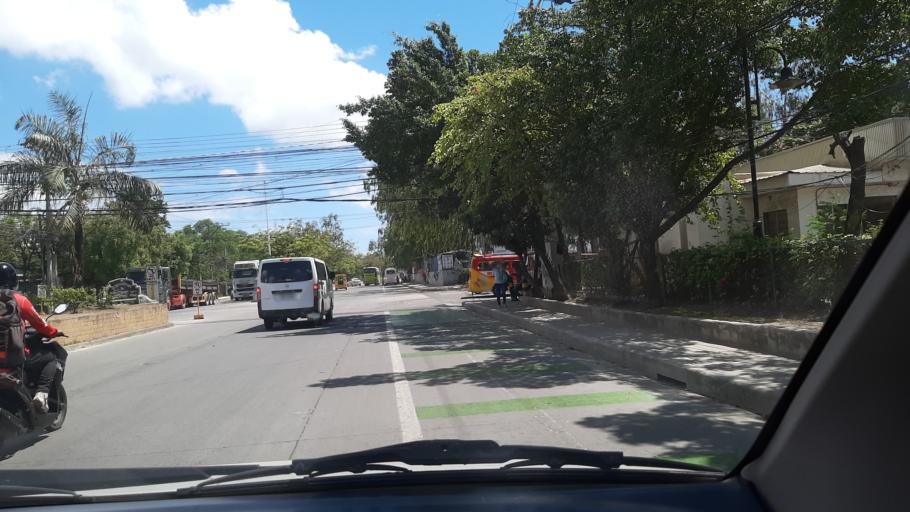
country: PH
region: Central Visayas
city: Mandaue City
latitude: 10.3264
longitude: 123.9344
